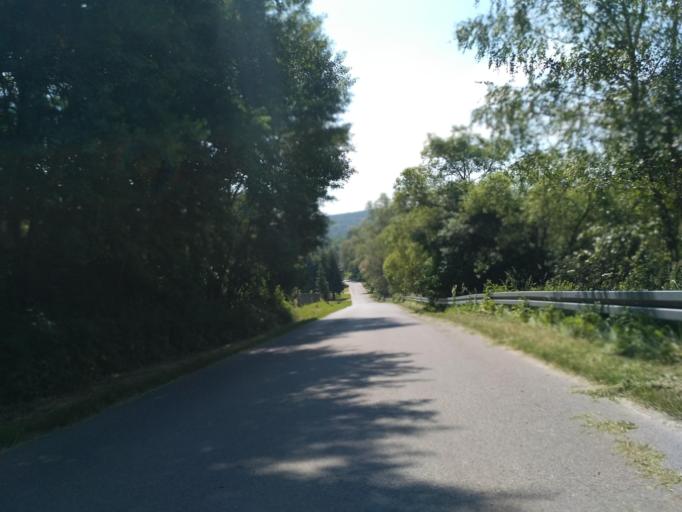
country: PL
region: Subcarpathian Voivodeship
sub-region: Powiat brzozowski
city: Golcowa
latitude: 49.8134
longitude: 22.0489
